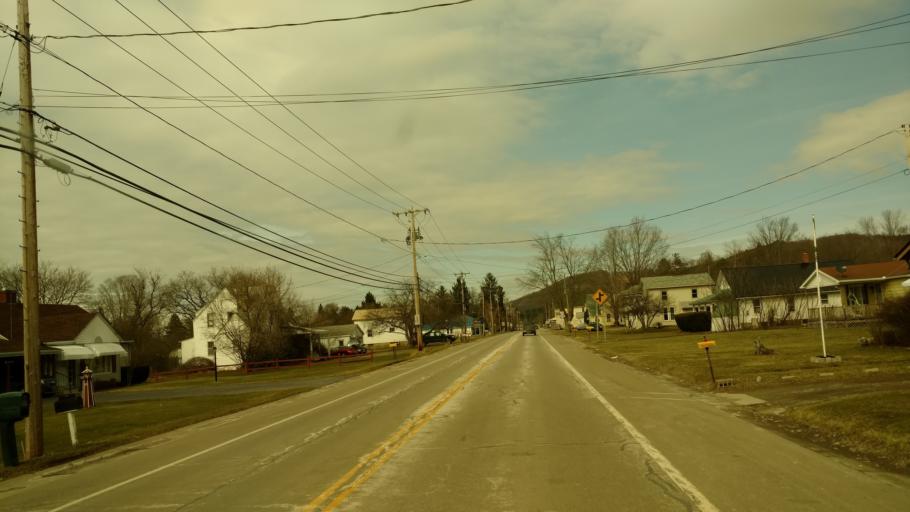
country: US
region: New York
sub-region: Allegany County
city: Wellsville
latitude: 42.0837
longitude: -77.9215
